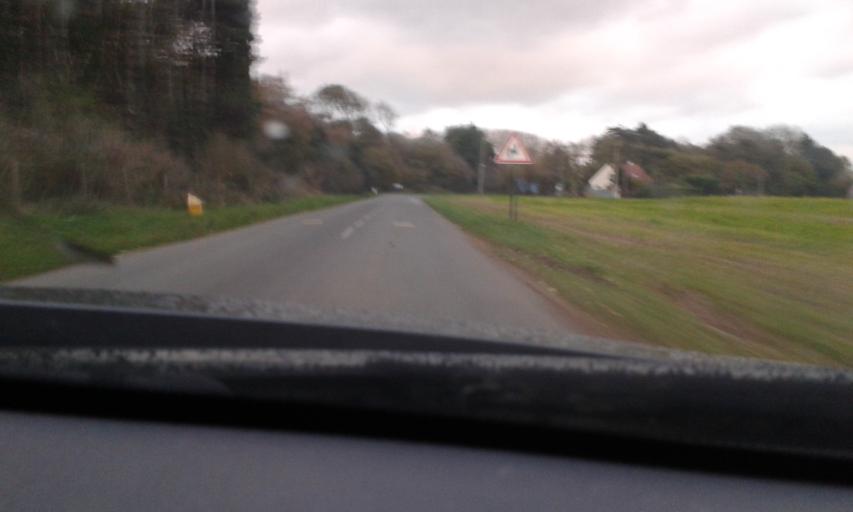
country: FR
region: Nord-Pas-de-Calais
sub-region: Departement du Pas-de-Calais
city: Ferques
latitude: 50.8771
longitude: 1.7678
